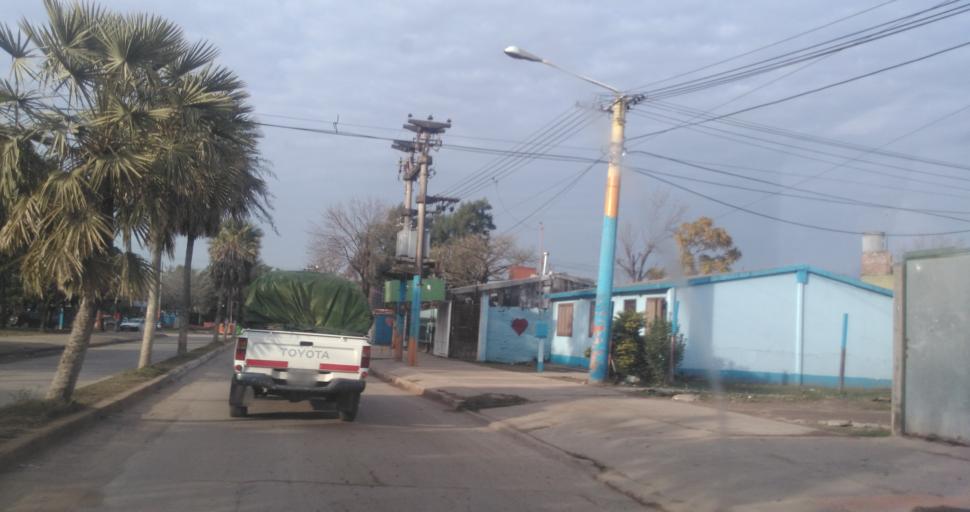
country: AR
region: Chaco
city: Resistencia
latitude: -27.4848
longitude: -58.9891
